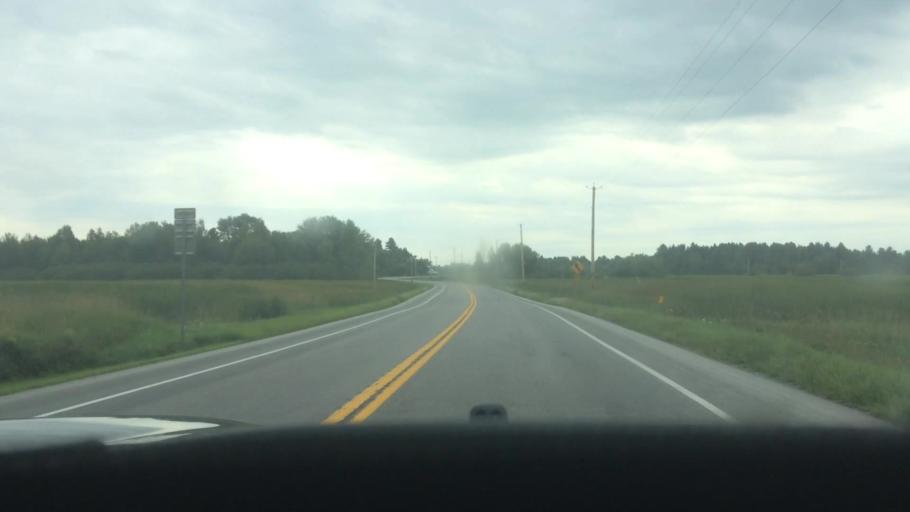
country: US
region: New York
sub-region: St. Lawrence County
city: Ogdensburg
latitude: 44.5807
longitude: -75.3692
